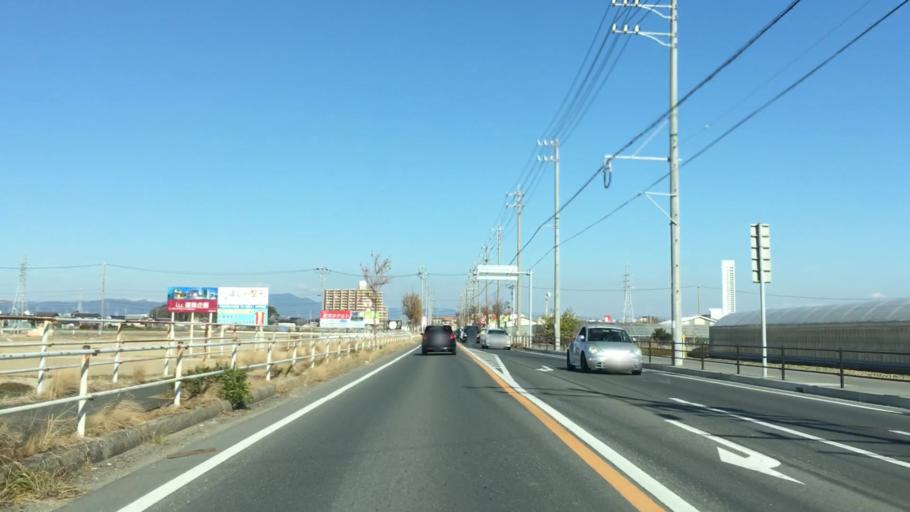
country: JP
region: Aichi
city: Toyohashi
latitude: 34.7342
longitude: 137.3607
